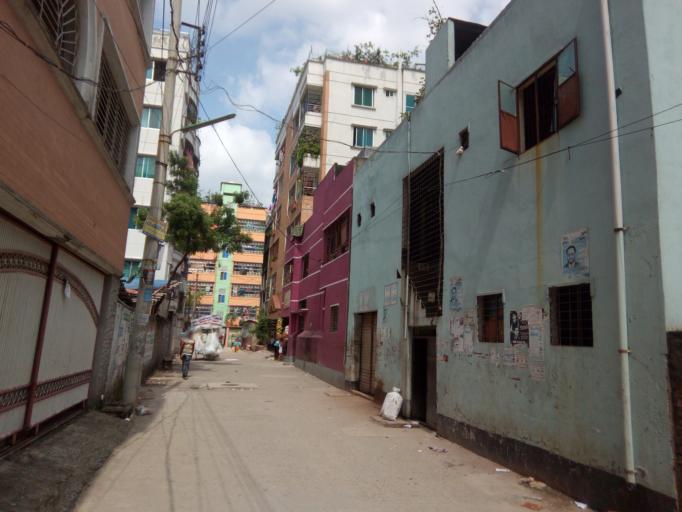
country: BD
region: Dhaka
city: Azimpur
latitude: 23.7405
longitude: 90.3622
